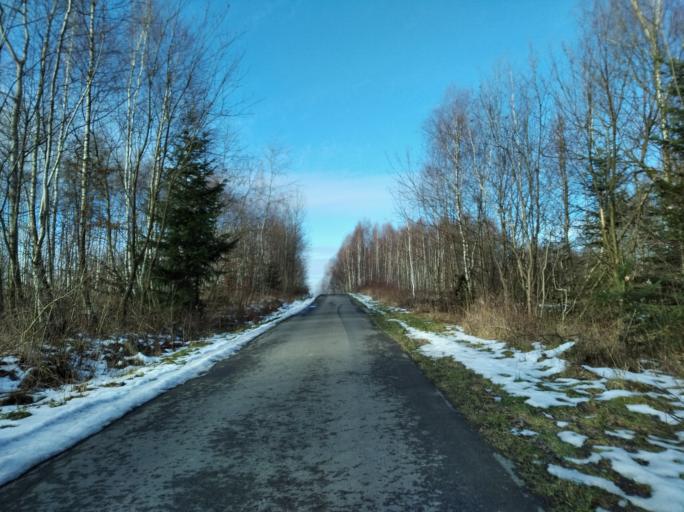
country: PL
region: Subcarpathian Voivodeship
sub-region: Powiat strzyzowski
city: Gwoznica Gorna
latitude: 49.8220
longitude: 21.9876
